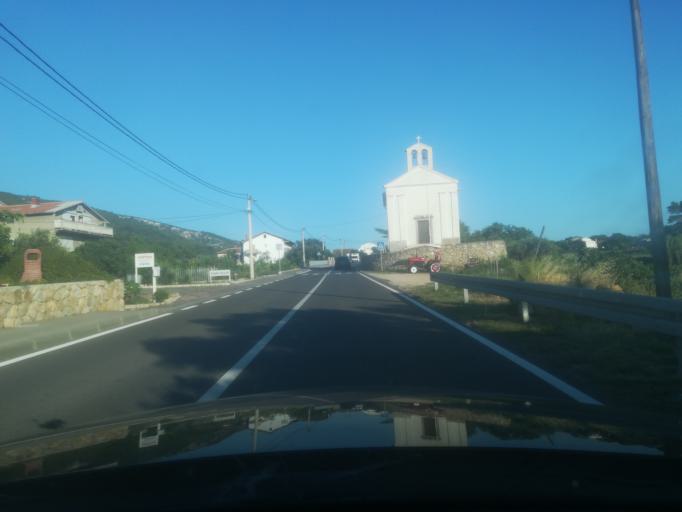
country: HR
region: Primorsko-Goranska
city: Banjol
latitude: 44.7711
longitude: 14.7627
